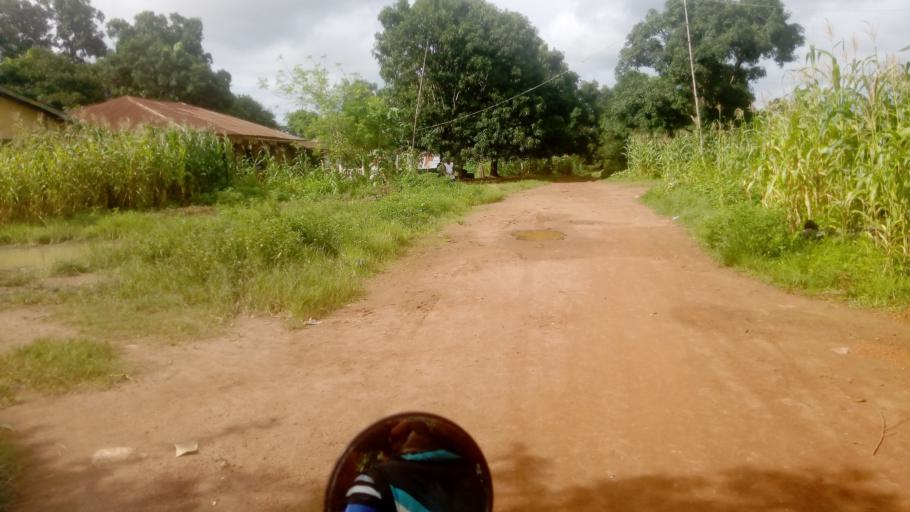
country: SL
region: Northern Province
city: Port Loko
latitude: 8.7093
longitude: -12.6800
